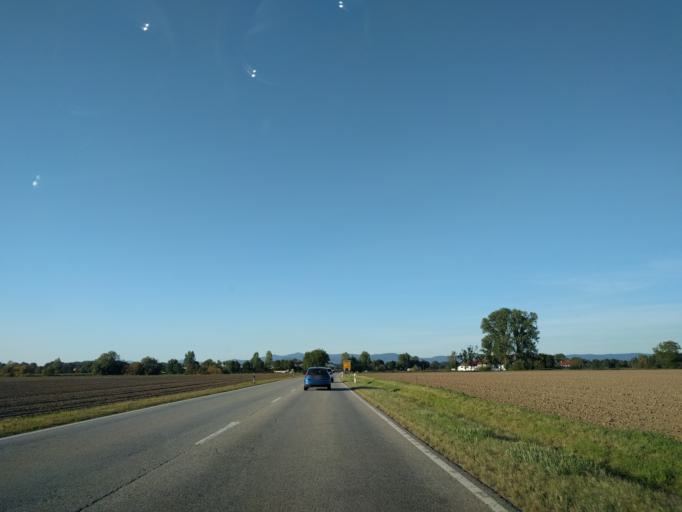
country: DE
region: Bavaria
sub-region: Lower Bavaria
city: Osterhofen
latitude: 48.7070
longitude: 13.0455
